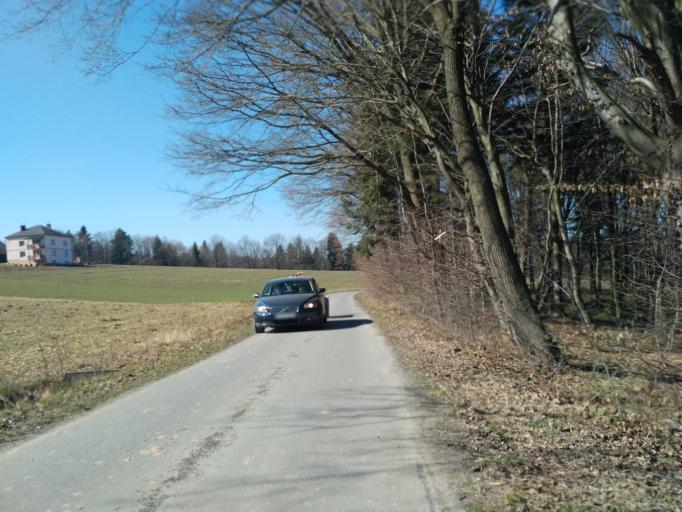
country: PL
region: Subcarpathian Voivodeship
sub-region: Powiat ropczycko-sedziszowski
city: Wielopole Skrzynskie
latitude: 49.9505
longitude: 21.5851
